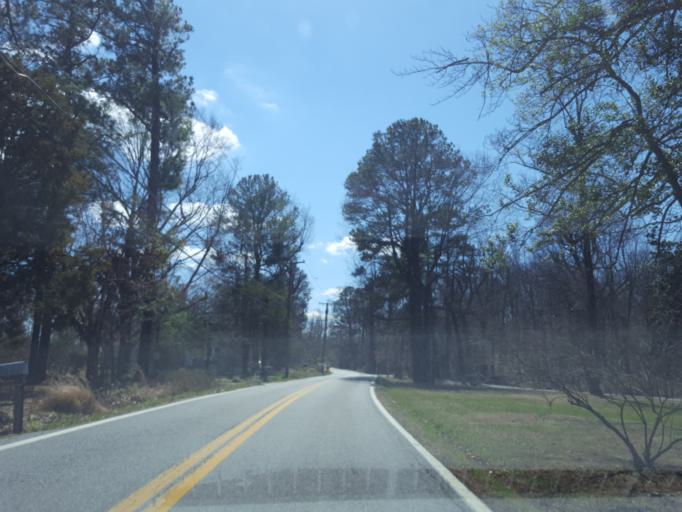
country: US
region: Maryland
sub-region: Calvert County
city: North Beach
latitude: 38.7223
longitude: -76.5278
